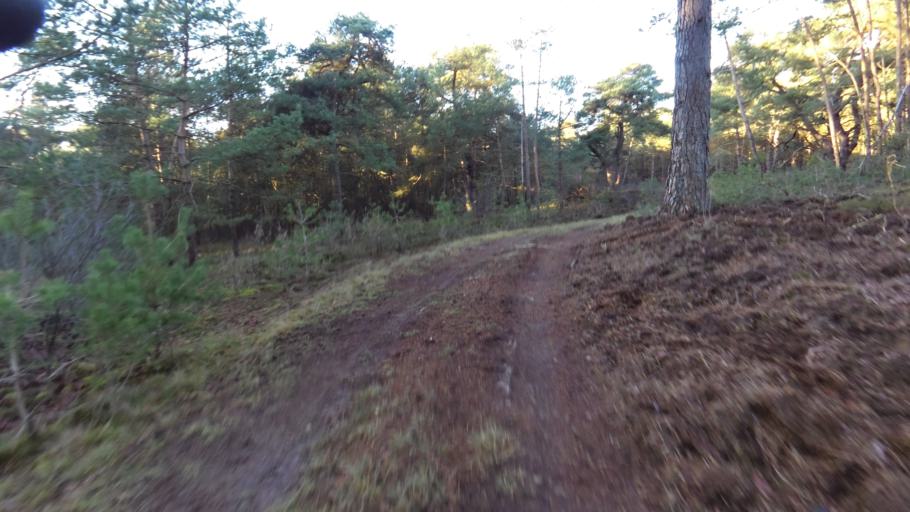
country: NL
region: Gelderland
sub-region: Gemeente Barneveld
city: Garderen
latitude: 52.1993
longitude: 5.7417
